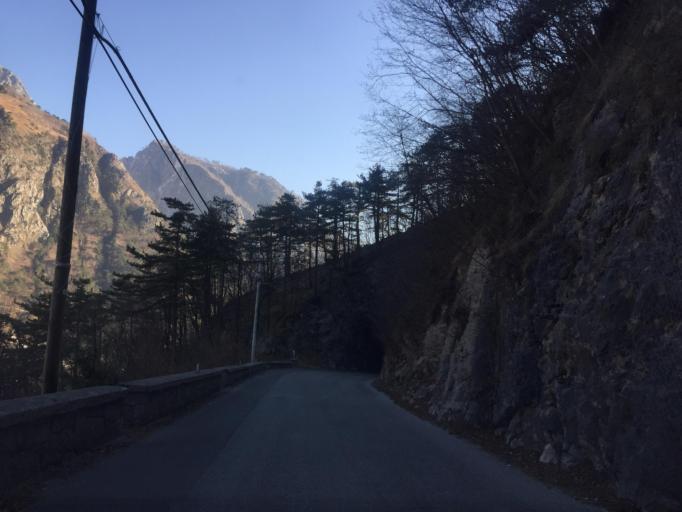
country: IT
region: Friuli Venezia Giulia
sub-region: Provincia di Udine
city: Tolmezzo
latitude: 46.4141
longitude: 13.0471
